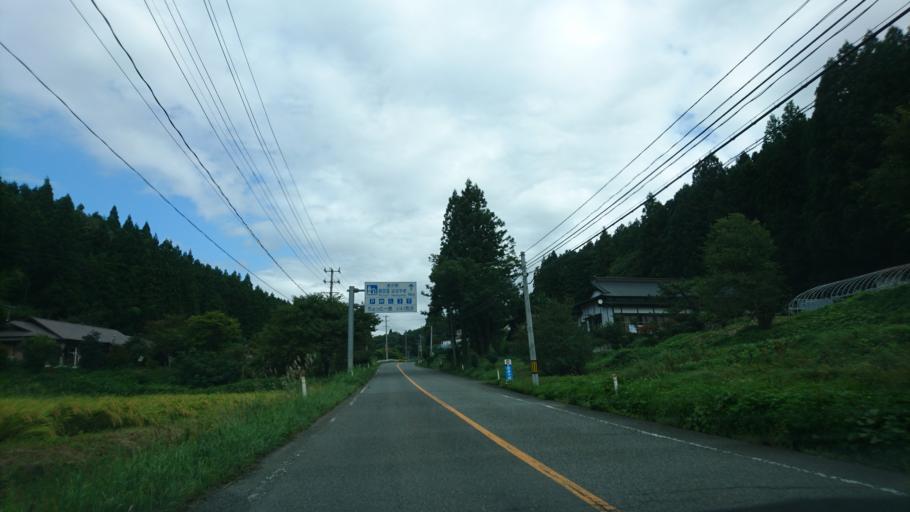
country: JP
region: Miyagi
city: Furukawa
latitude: 38.7683
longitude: 140.8629
